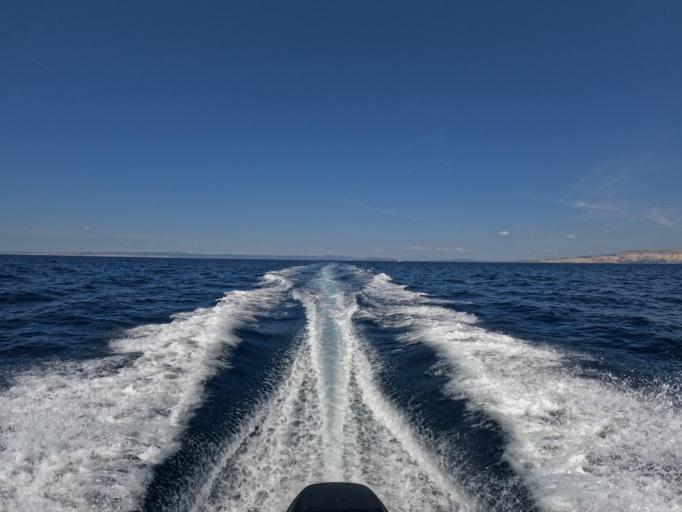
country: HR
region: Primorsko-Goranska
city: Lopar
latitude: 44.8656
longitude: 14.6798
